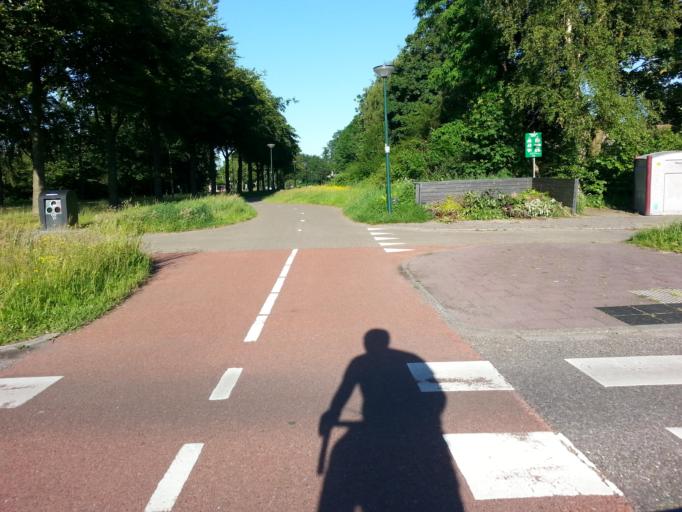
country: NL
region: Utrecht
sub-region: Gemeente Leusden
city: Leusden
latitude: 52.1323
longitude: 5.4347
